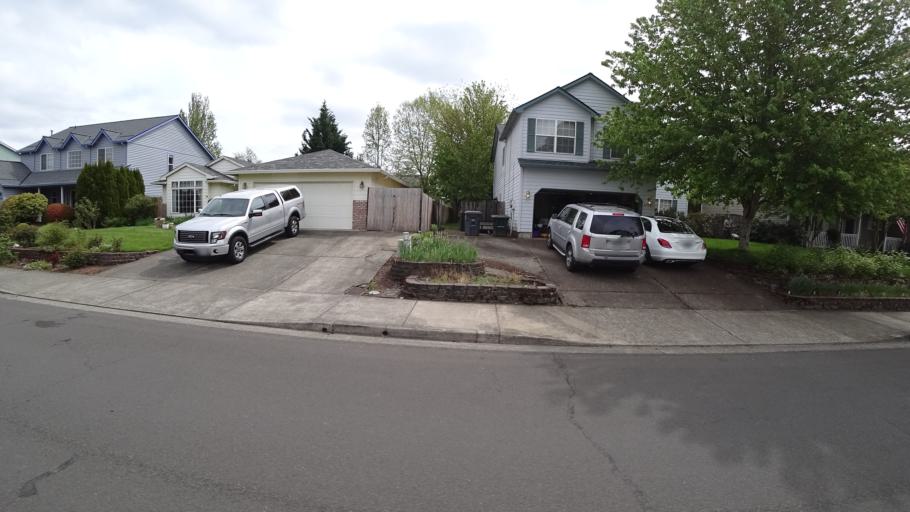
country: US
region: Oregon
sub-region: Washington County
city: Hillsboro
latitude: 45.5480
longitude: -122.9926
